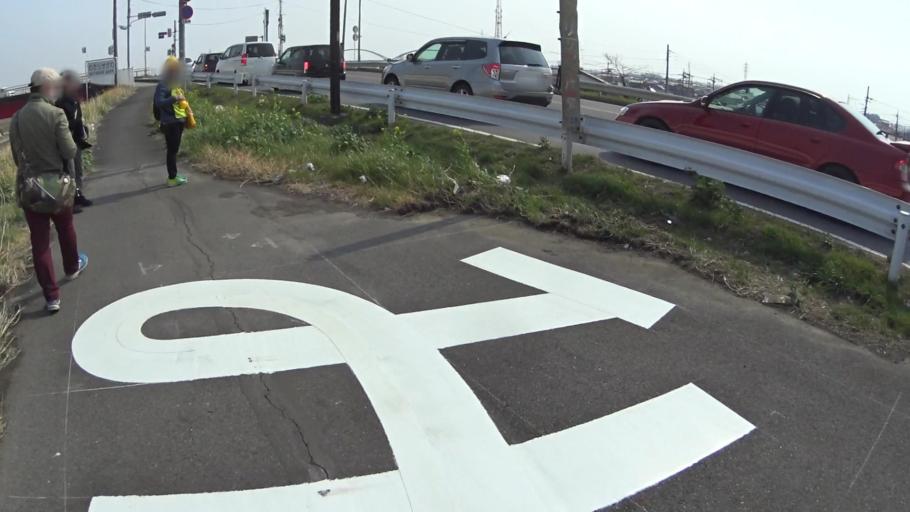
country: JP
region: Ibaraki
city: Koga
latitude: 36.1929
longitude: 139.6889
